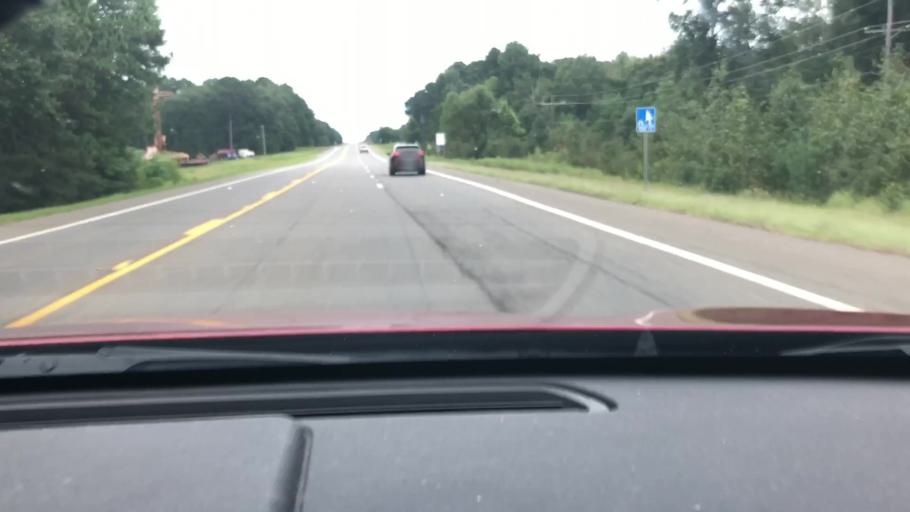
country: US
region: Arkansas
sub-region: Lafayette County
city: Stamps
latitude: 33.3643
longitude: -93.4721
